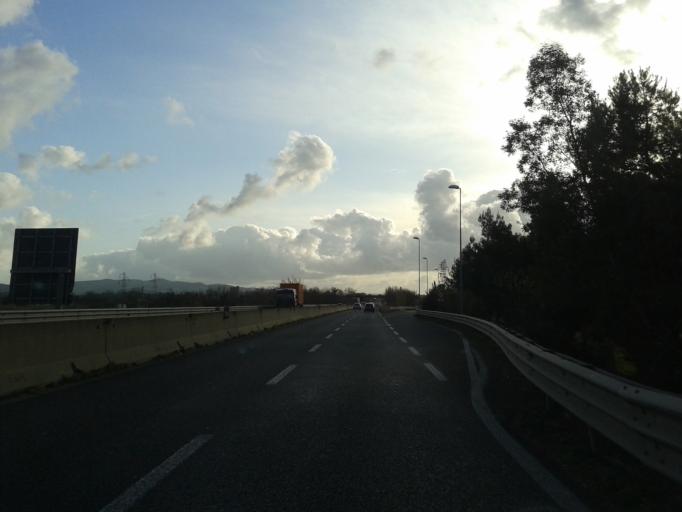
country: IT
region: Tuscany
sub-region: Provincia di Livorno
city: Livorno
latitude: 43.5583
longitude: 10.3453
